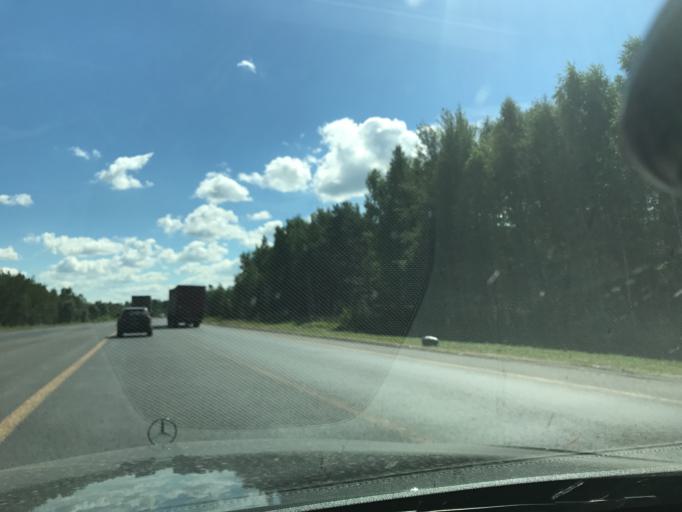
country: RU
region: Nizjnij Novgorod
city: Gorbatovka
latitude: 56.2934
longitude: 43.6954
